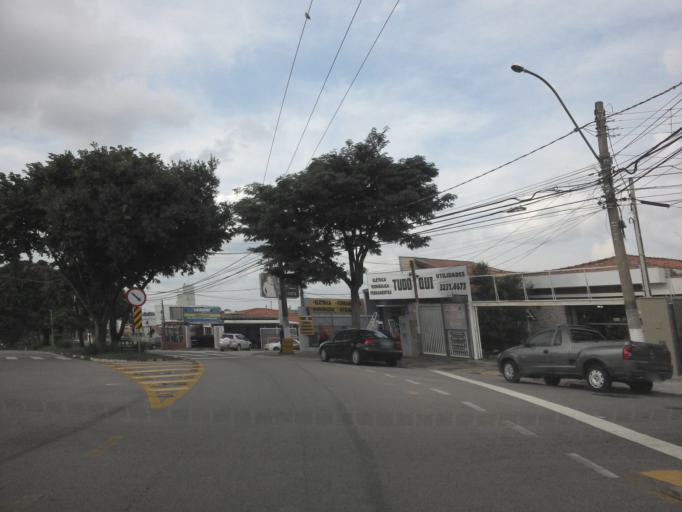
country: BR
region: Sao Paulo
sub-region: Campinas
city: Campinas
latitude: -22.9175
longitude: -47.0498
